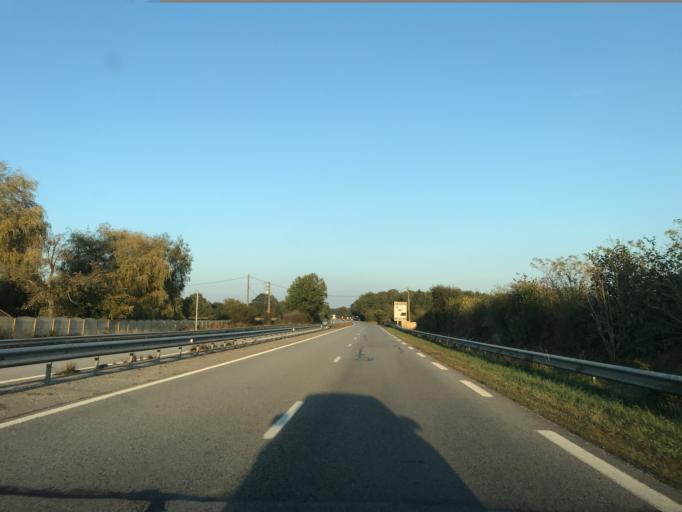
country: FR
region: Pays de la Loire
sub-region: Departement de la Sarthe
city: Mamers
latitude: 48.5050
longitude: 0.3155
